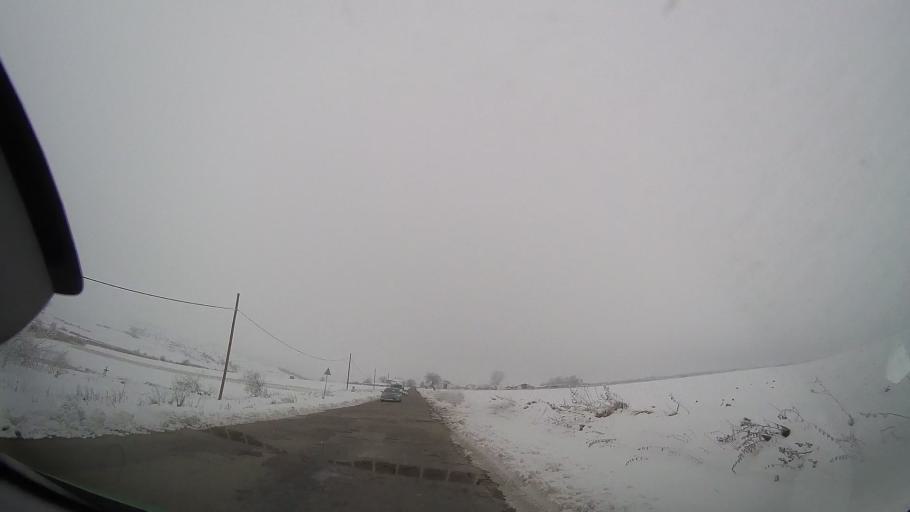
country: RO
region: Neamt
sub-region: Comuna Icusesti
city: Balusesti
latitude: 46.8553
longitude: 27.0334
